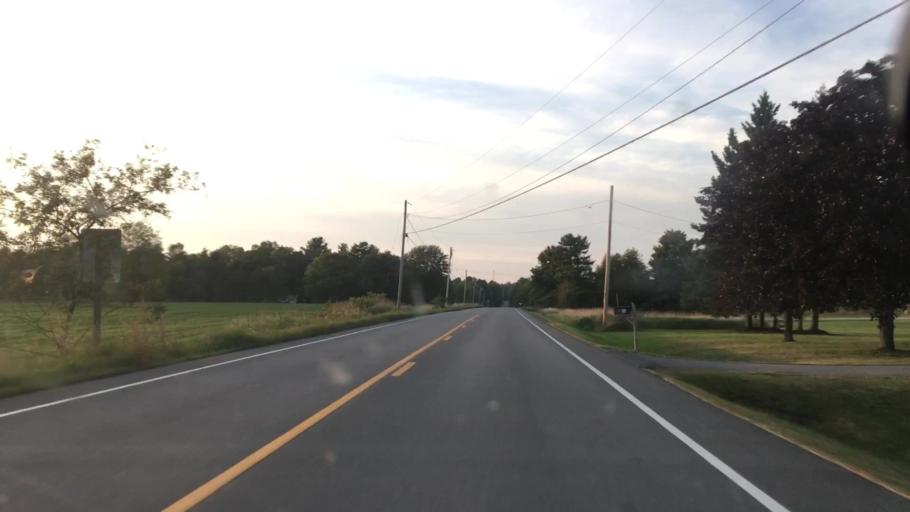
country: US
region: Maine
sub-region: Penobscot County
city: Hermon
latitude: 44.7462
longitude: -68.9671
